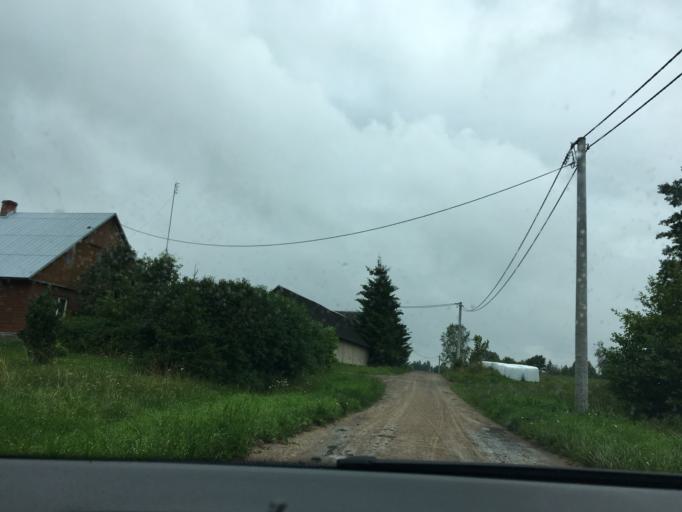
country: PL
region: Podlasie
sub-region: Powiat sejnenski
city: Krasnopol
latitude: 54.0943
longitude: 23.2704
